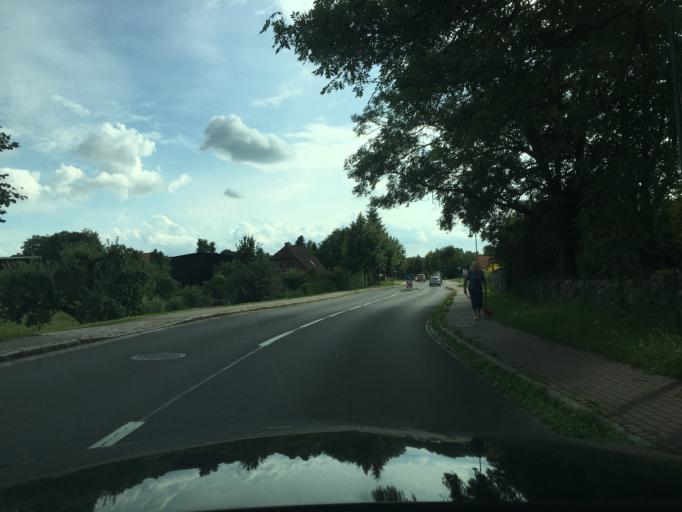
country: DE
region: Mecklenburg-Vorpommern
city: Penzlin
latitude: 53.4466
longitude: 13.0531
